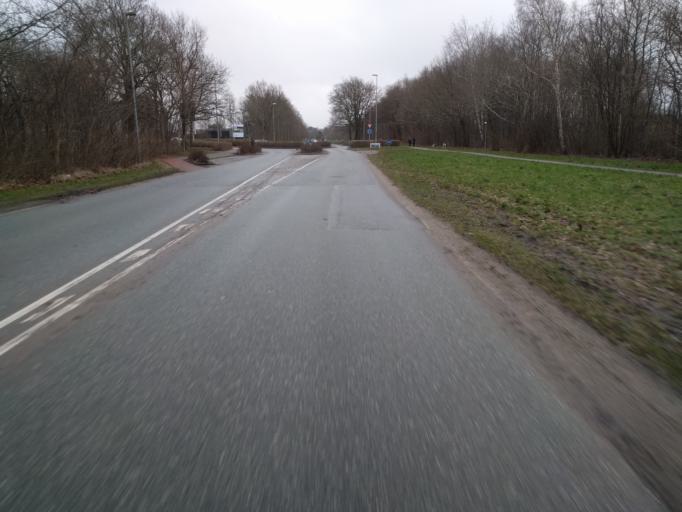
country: DK
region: Central Jutland
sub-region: Viborg Kommune
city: Viborg
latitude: 56.4631
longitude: 9.4466
